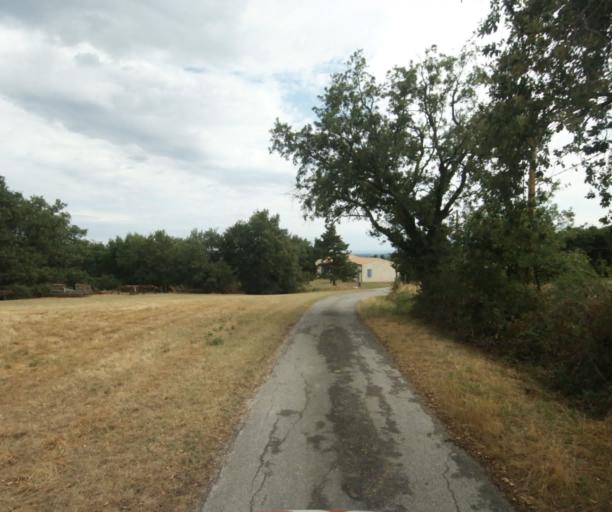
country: FR
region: Midi-Pyrenees
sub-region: Departement de la Haute-Garonne
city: Revel
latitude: 43.4404
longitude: 1.9843
